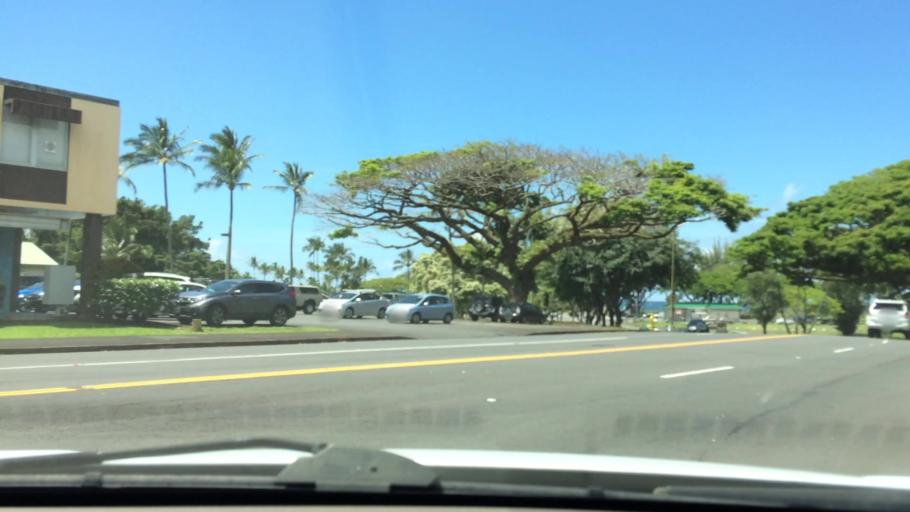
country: US
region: Hawaii
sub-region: Hawaii County
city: Hilo
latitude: 19.7197
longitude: -155.0791
